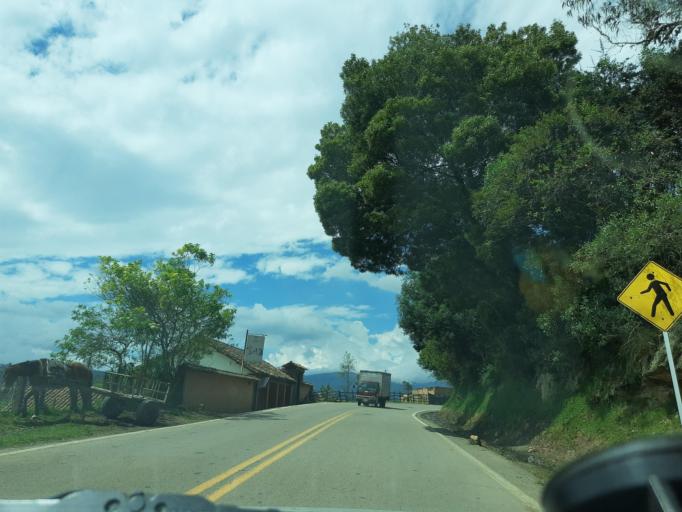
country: CO
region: Boyaca
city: Chiquinquira
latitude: 5.6150
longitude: -73.7451
